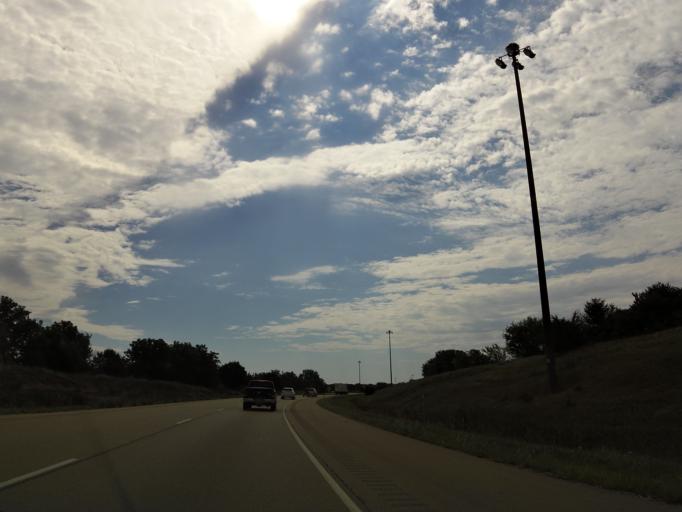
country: US
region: Illinois
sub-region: McLean County
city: Normal
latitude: 40.5386
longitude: -89.0141
